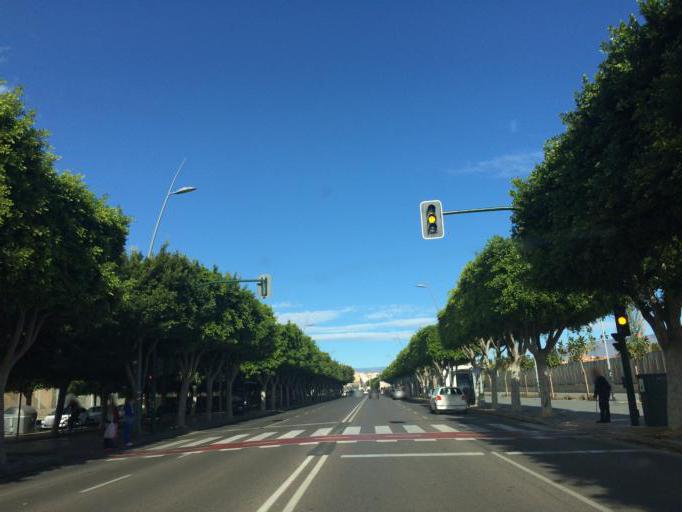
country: ES
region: Andalusia
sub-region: Provincia de Almeria
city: Almeria
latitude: 36.8296
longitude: -2.4458
